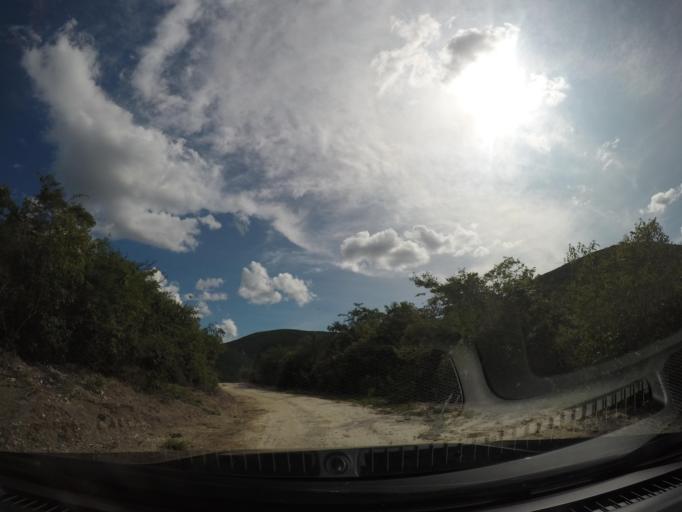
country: BR
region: Bahia
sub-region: Barra Da Estiva
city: Barra da Estiva
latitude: -13.1450
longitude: -41.5985
